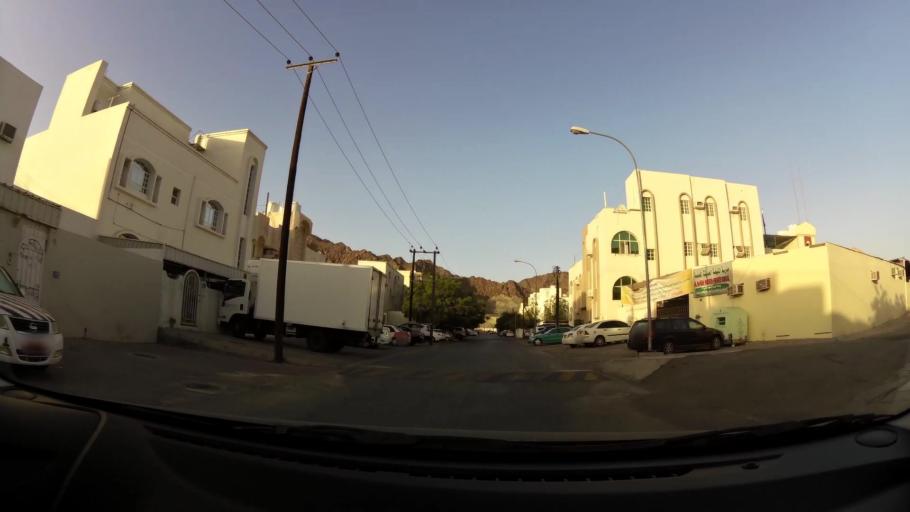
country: OM
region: Muhafazat Masqat
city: Muscat
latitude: 23.5736
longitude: 58.5725
